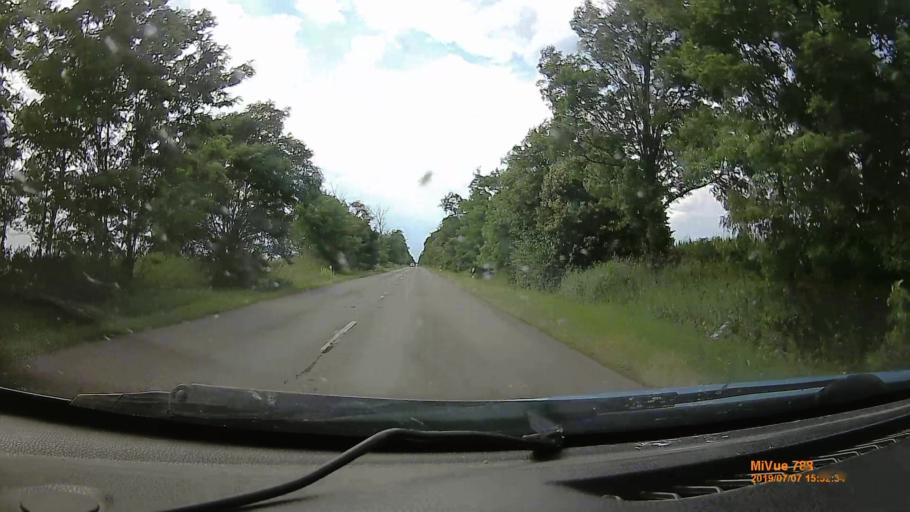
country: HU
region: Pest
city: Szentlorinckata
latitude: 47.5421
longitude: 19.8207
